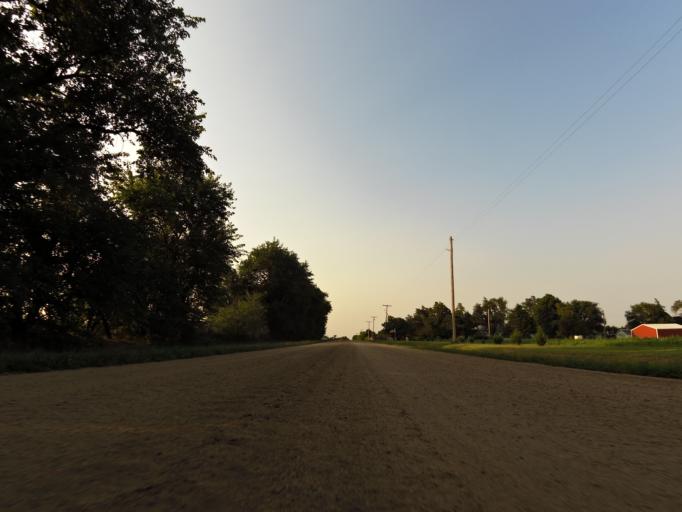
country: US
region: Kansas
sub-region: Reno County
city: South Hutchinson
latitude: 37.9979
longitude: -97.9955
